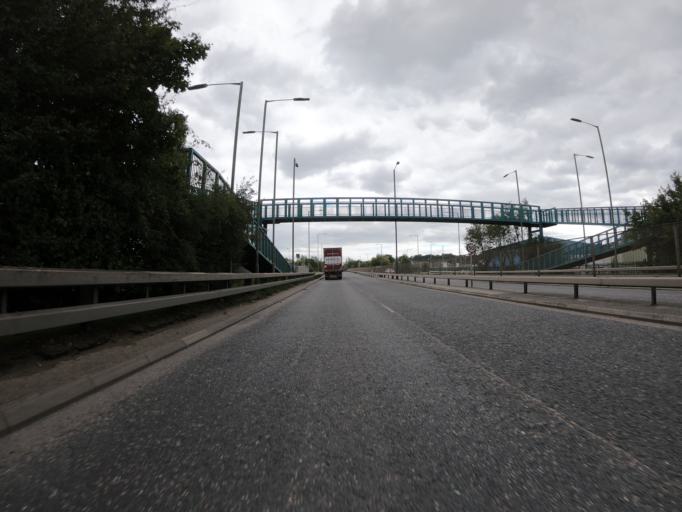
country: GB
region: England
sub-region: Greater London
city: Belvedere
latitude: 51.4950
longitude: 0.1603
